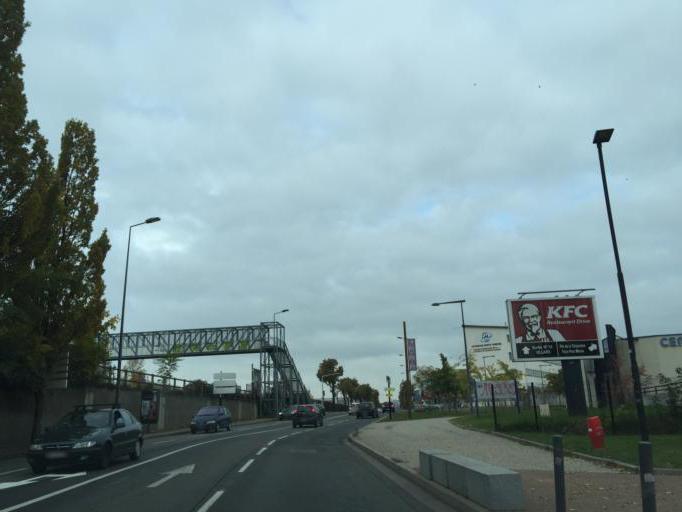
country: FR
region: Rhone-Alpes
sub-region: Departement de la Loire
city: Saint-Etienne
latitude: 45.4500
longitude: 4.3902
